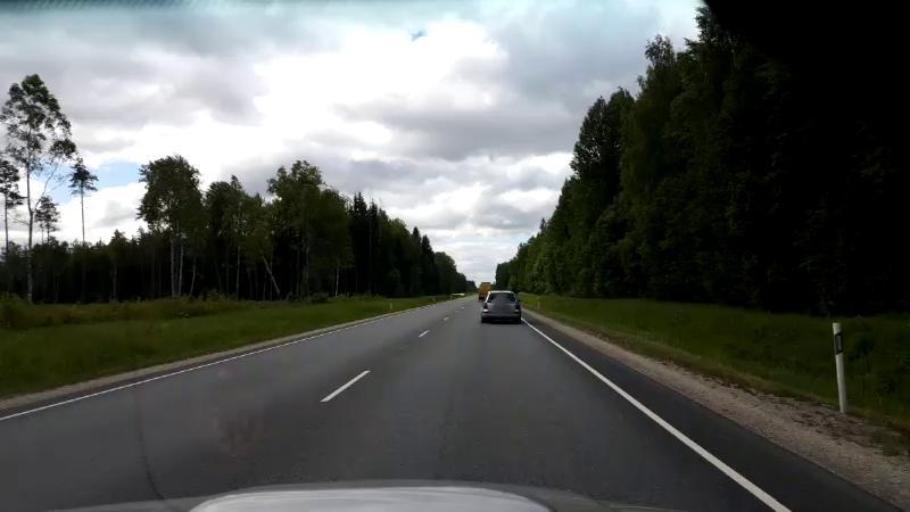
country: EE
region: Raplamaa
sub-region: Maerjamaa vald
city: Marjamaa
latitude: 58.7892
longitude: 24.4130
